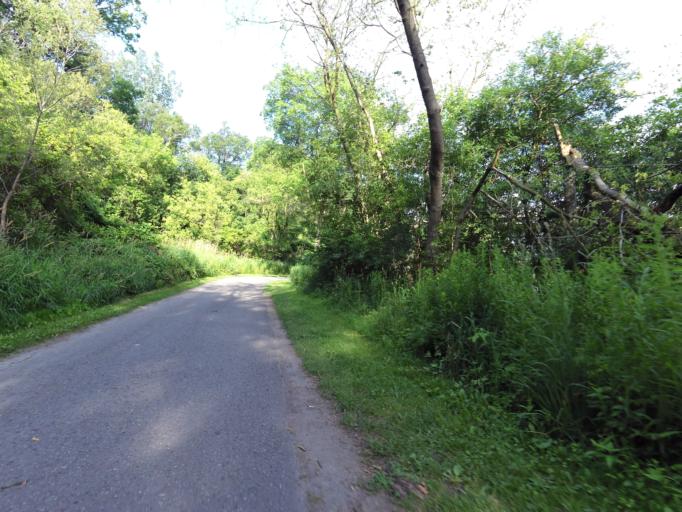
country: CA
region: Ontario
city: Etobicoke
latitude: 43.6633
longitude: -79.5066
